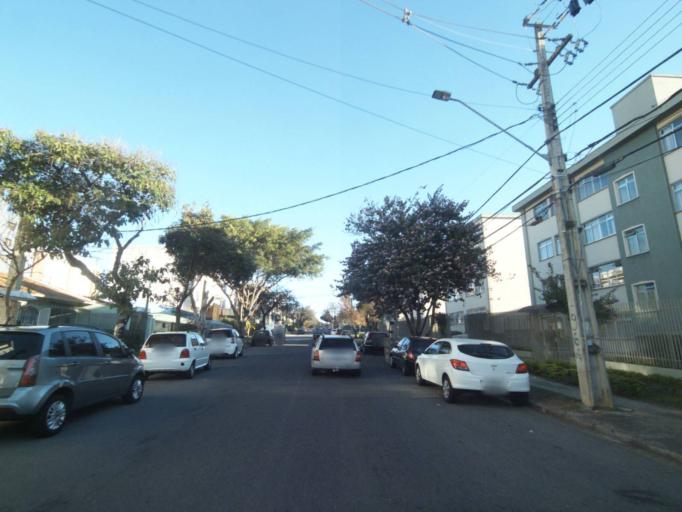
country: BR
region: Parana
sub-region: Curitiba
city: Curitiba
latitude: -25.4579
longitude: -49.2960
